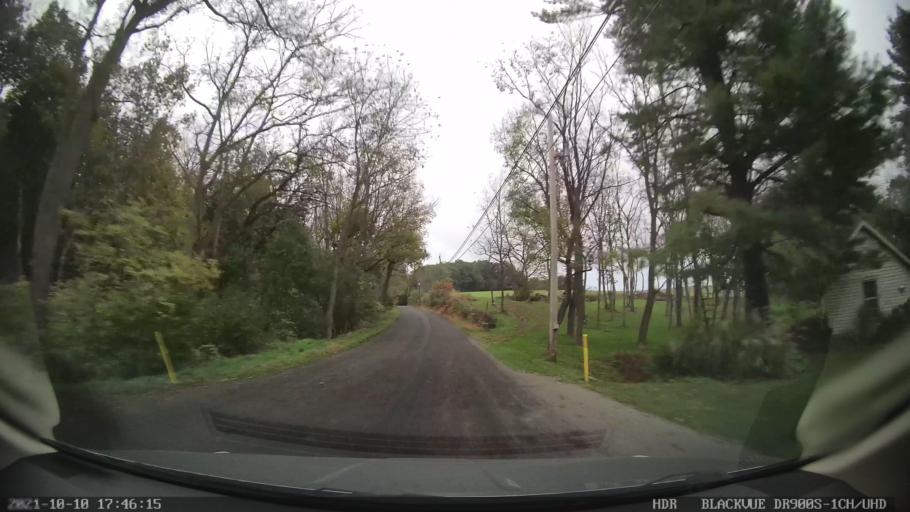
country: US
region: Pennsylvania
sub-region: Lehigh County
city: Breinigsville
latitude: 40.5611
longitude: -75.6748
